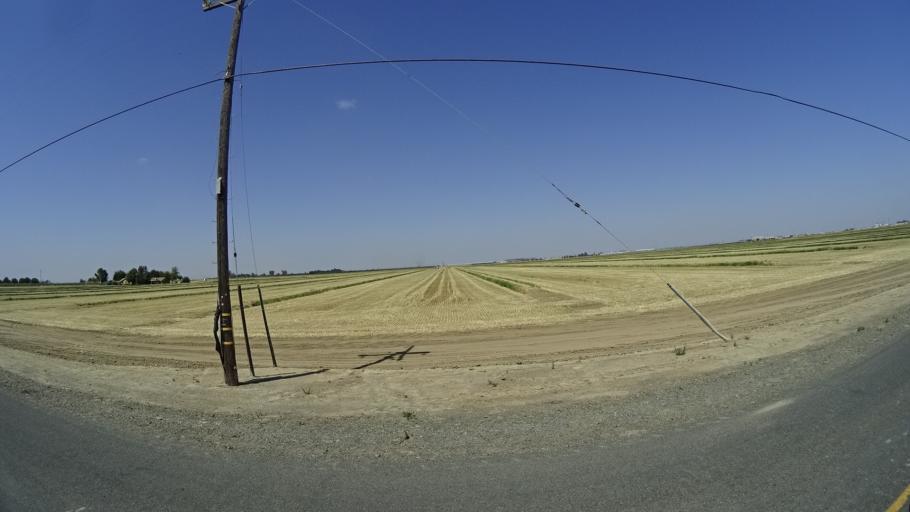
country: US
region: California
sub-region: Kings County
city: Home Garden
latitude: 36.2477
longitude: -119.6189
